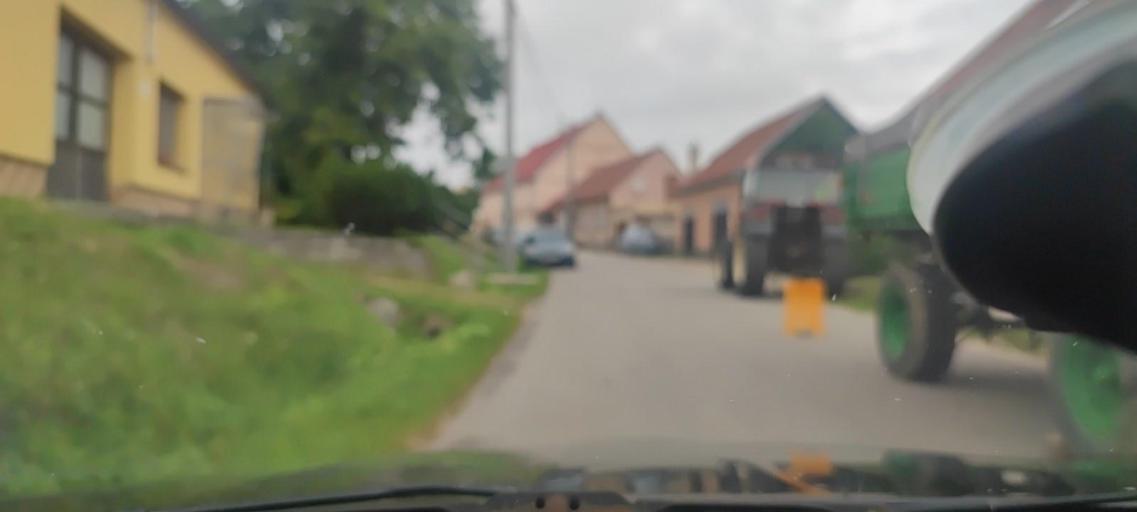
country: CZ
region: South Moravian
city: Hosteradice
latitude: 48.9624
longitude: 16.2260
